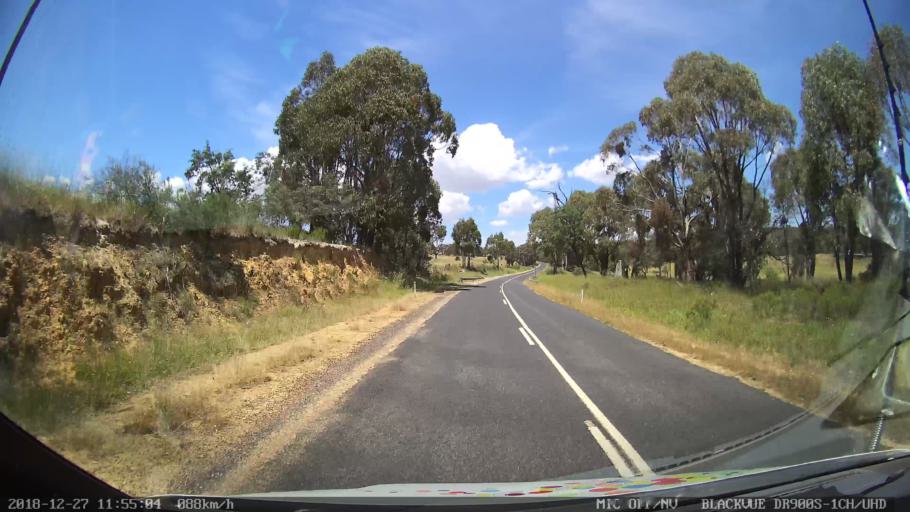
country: AU
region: New South Wales
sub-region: Blayney
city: Blayney
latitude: -33.6831
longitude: 149.4006
